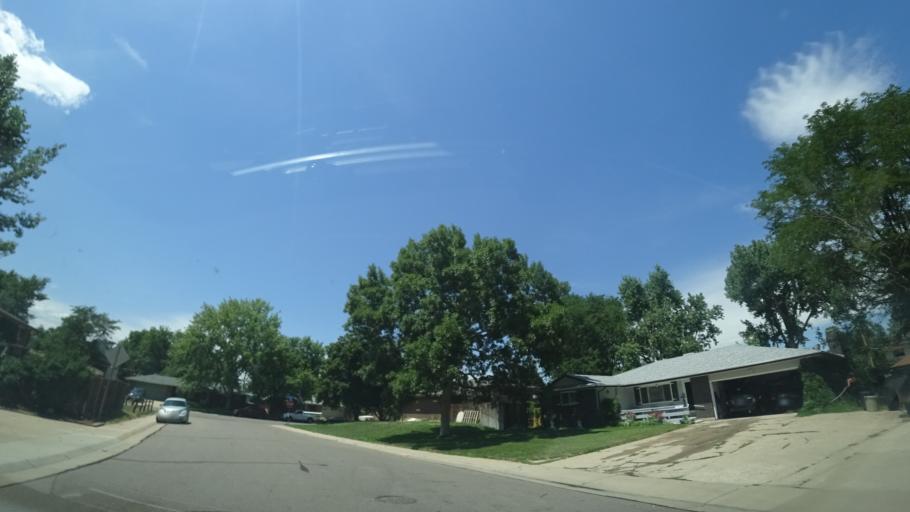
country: US
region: Colorado
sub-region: Jefferson County
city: Lakewood
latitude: 39.6952
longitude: -105.0940
